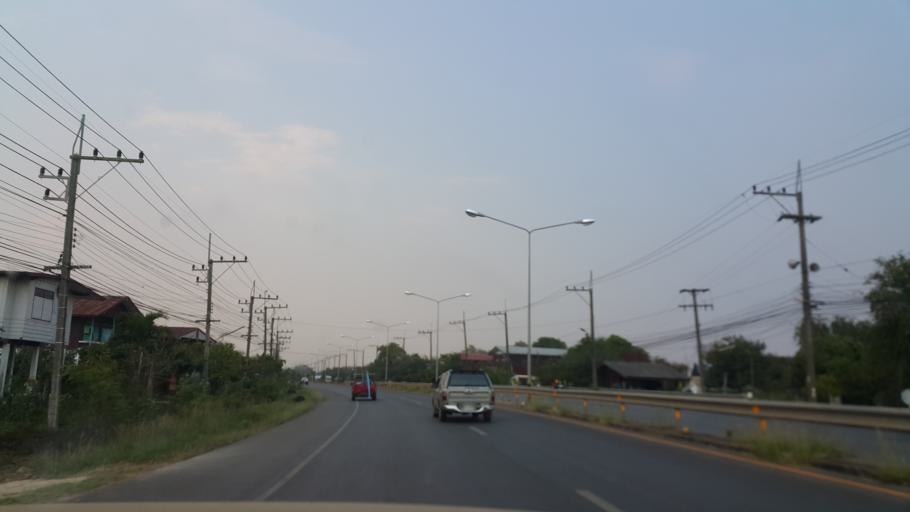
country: TH
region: Nakhon Phanom
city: That Phanom
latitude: 16.9839
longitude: 104.7279
